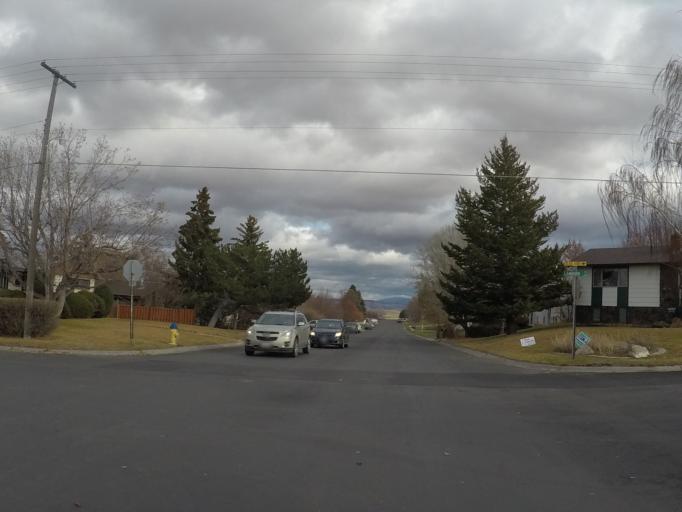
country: US
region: Montana
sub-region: Lewis and Clark County
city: Helena
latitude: 46.5814
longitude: -112.0091
